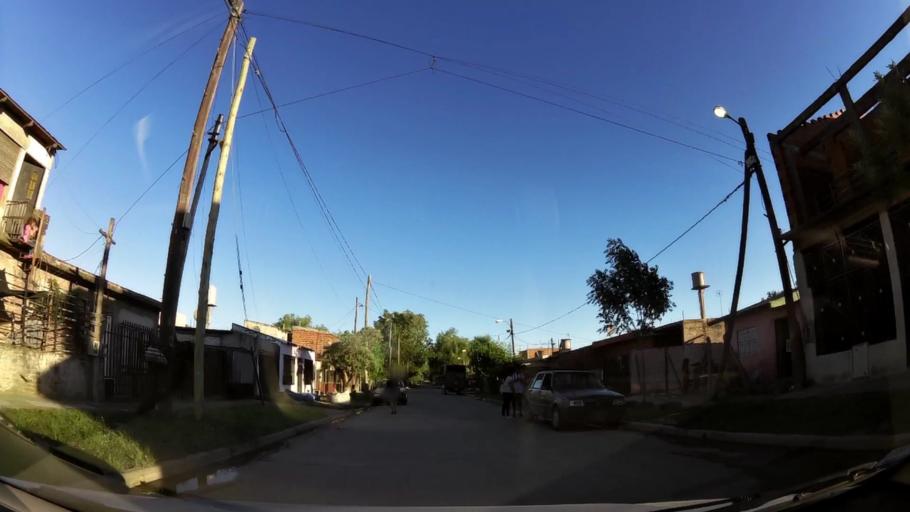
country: AR
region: Buenos Aires
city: San Justo
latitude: -34.7201
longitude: -58.6094
